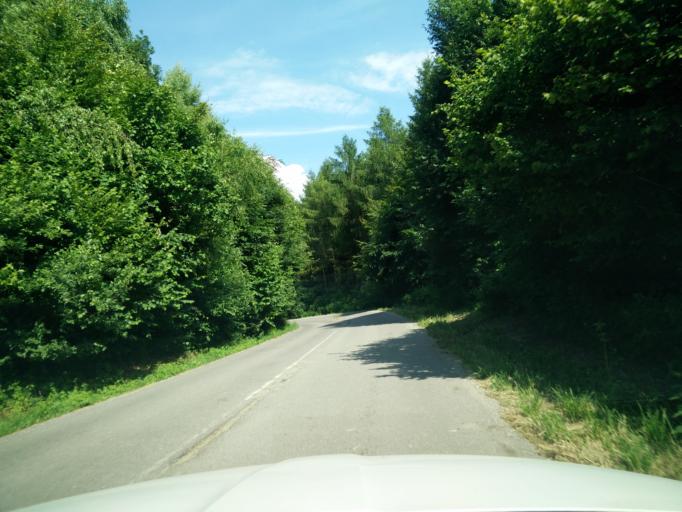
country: SK
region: Nitriansky
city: Bojnice
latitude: 48.8759
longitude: 18.5945
